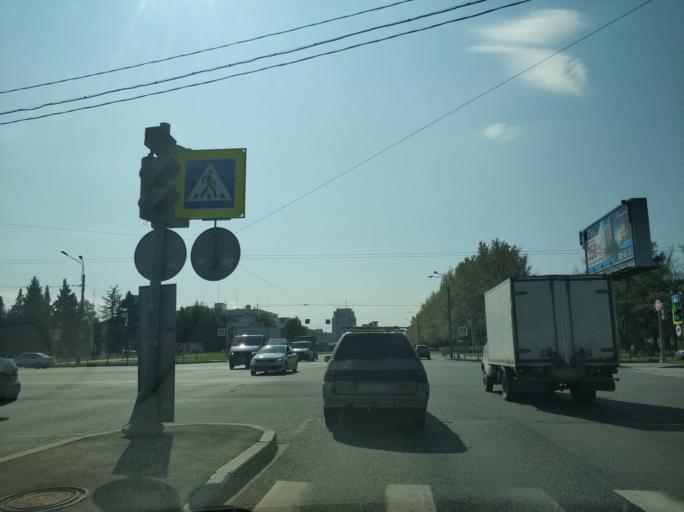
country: RU
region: St.-Petersburg
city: Kupchino
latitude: 59.8527
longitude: 30.3375
